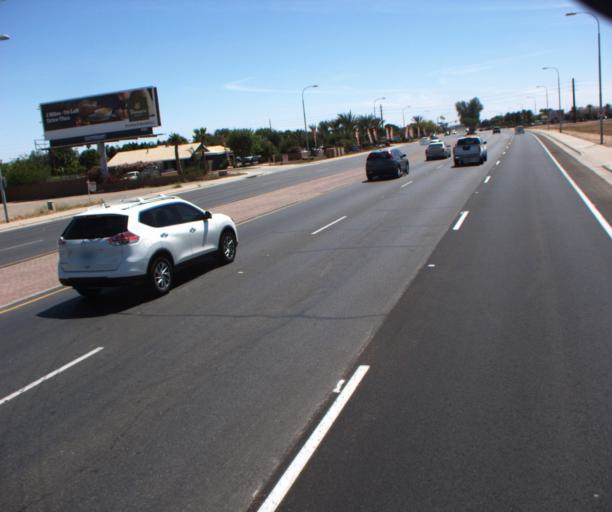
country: US
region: Arizona
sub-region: Maricopa County
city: Chandler
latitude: 33.2799
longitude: -111.8417
